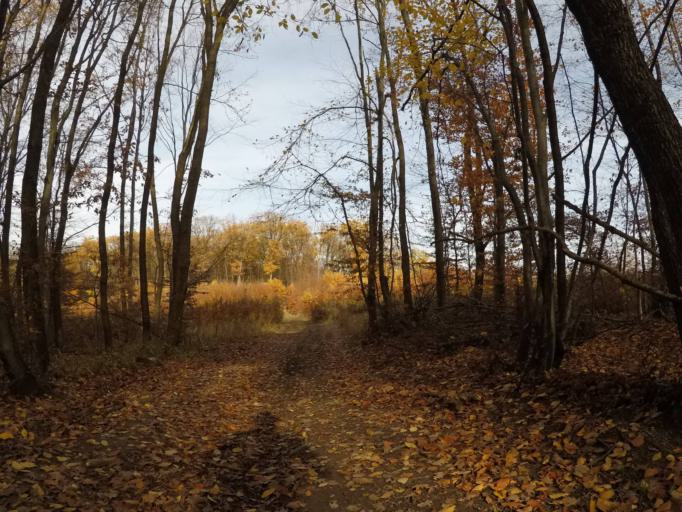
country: SK
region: Presovsky
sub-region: Okres Presov
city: Presov
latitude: 48.9302
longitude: 21.2218
